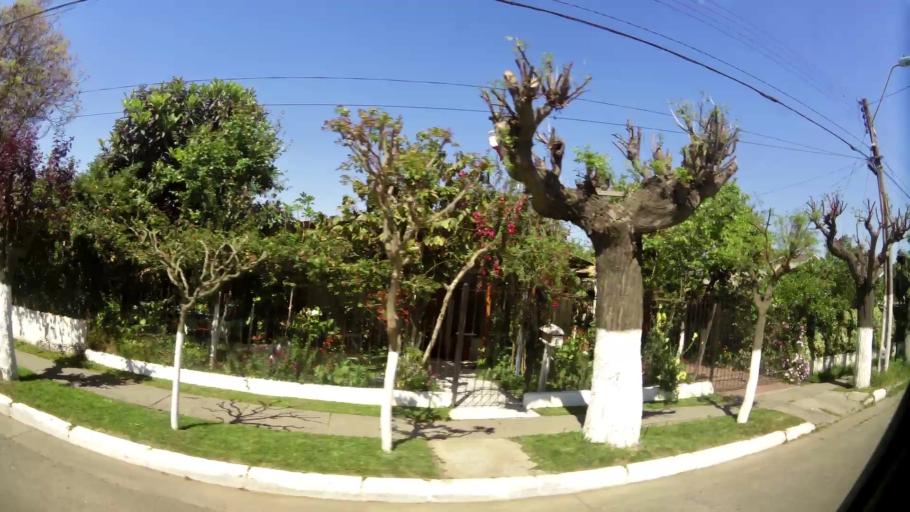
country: CL
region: Santiago Metropolitan
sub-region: Provincia de Talagante
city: Penaflor
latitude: -33.5720
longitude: -70.8084
